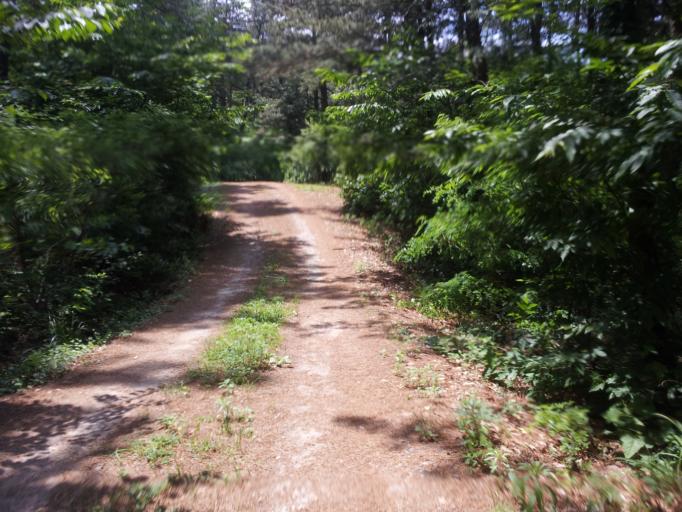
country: KR
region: Daejeon
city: Sintansin
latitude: 36.4405
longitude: 127.4892
